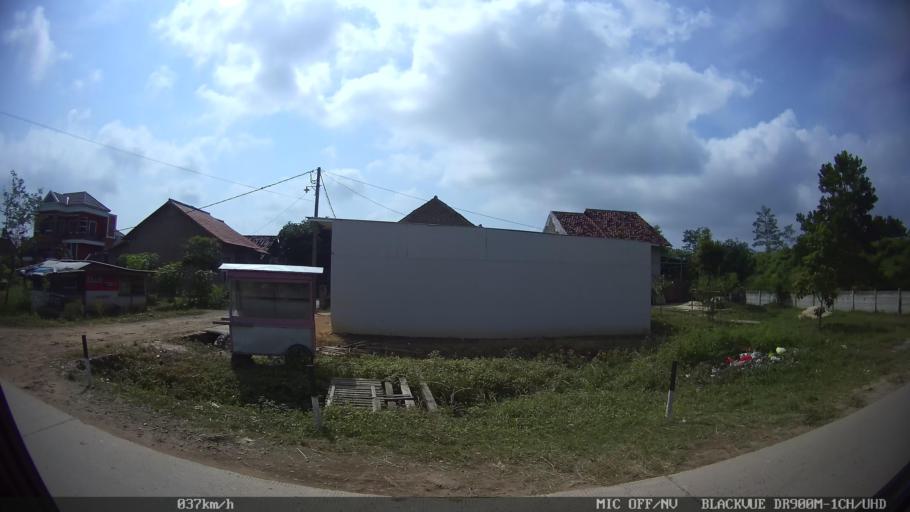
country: ID
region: Lampung
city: Kedaton
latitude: -5.3268
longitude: 105.2836
